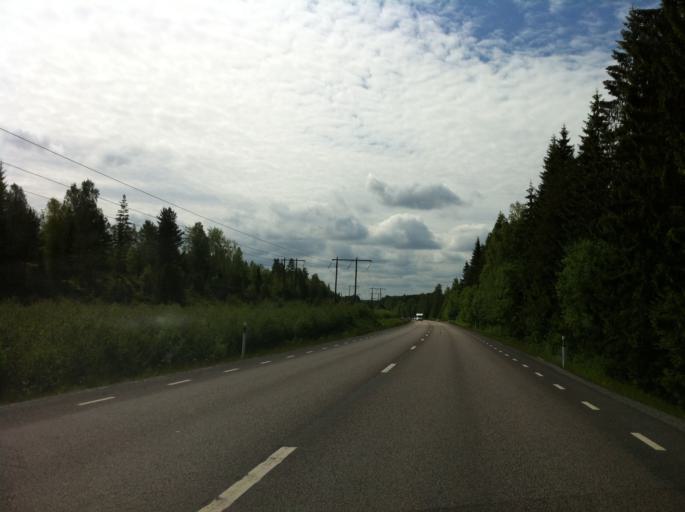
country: SE
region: Vaermland
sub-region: Karlstads Kommun
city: Edsvalla
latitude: 59.4153
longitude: 13.1856
